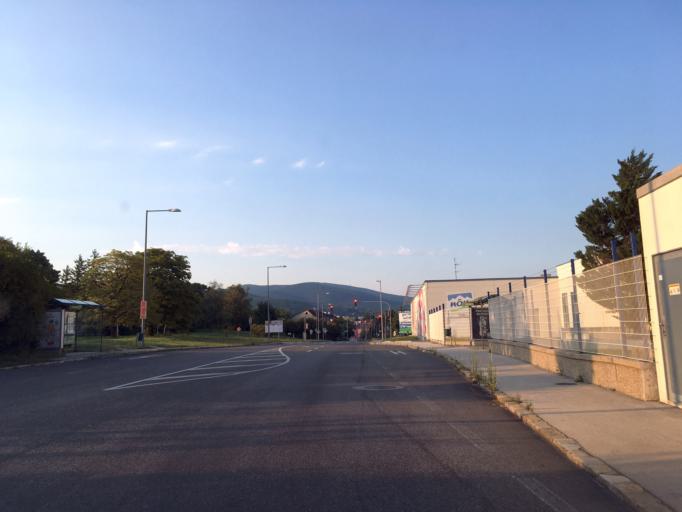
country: AT
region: Lower Austria
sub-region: Politischer Bezirk Baden
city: Baden
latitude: 47.9928
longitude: 16.2256
